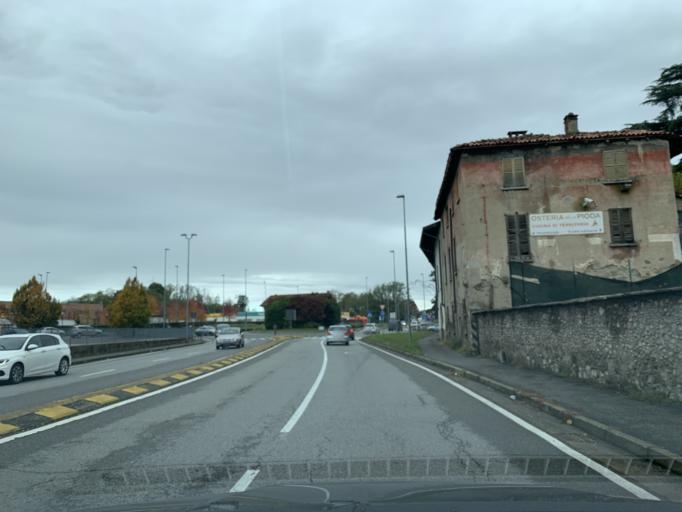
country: IT
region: Lombardy
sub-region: Provincia di Como
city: Vertemate Con Minoprio
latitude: 45.7254
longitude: 9.0678
